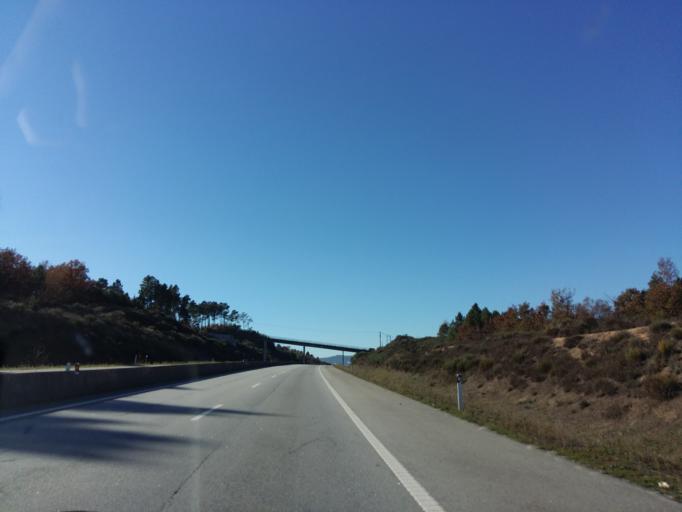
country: PT
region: Castelo Branco
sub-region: Covilha
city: Covilha
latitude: 40.2453
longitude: -7.4645
